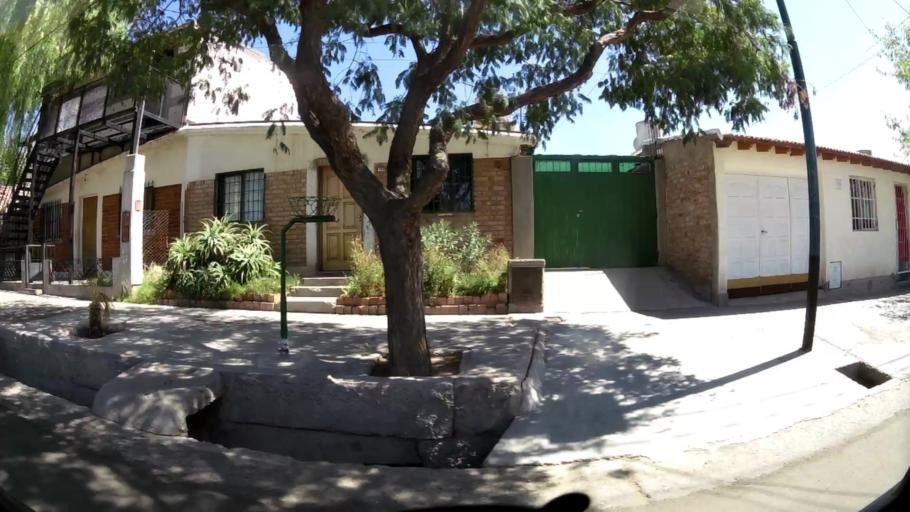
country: AR
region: Mendoza
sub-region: Departamento de Godoy Cruz
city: Godoy Cruz
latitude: -32.9488
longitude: -68.8691
